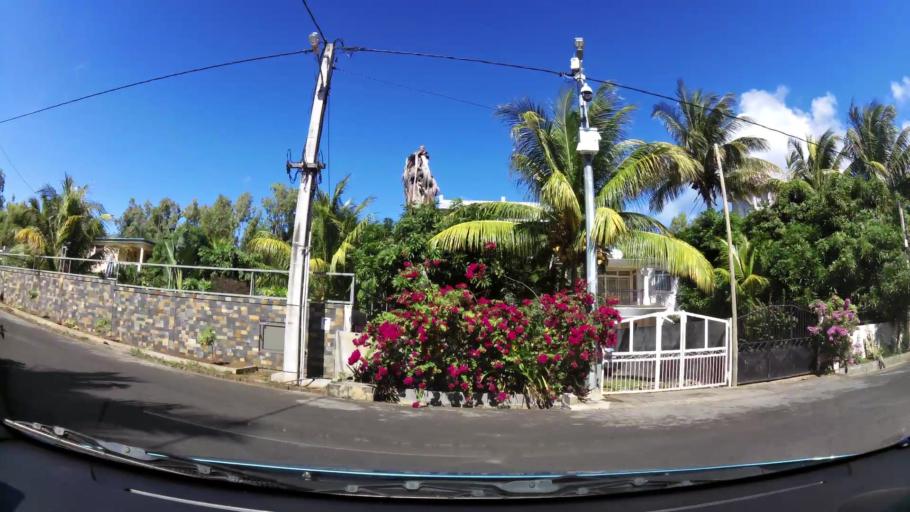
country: MU
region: Black River
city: Flic en Flac
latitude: -20.2855
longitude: 57.3710
